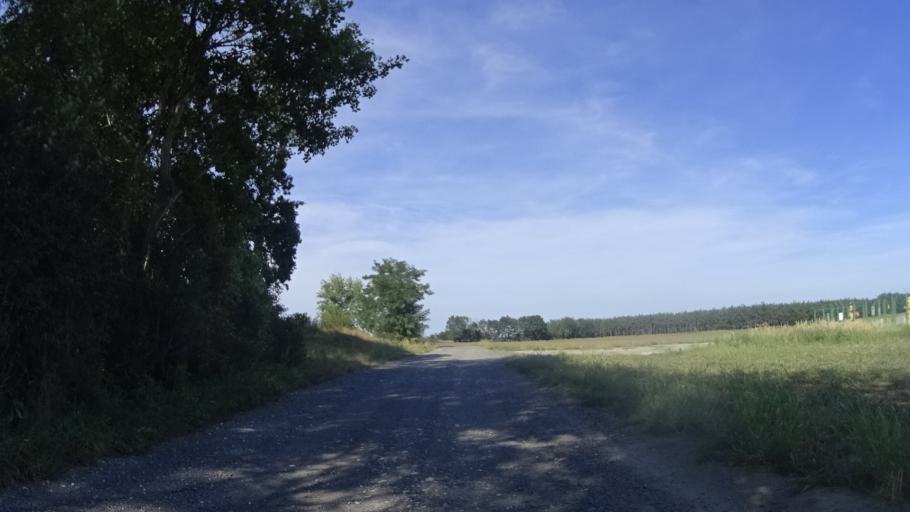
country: AT
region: Lower Austria
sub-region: Politischer Bezirk Ganserndorf
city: Durnkrut
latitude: 48.4305
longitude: 16.8680
